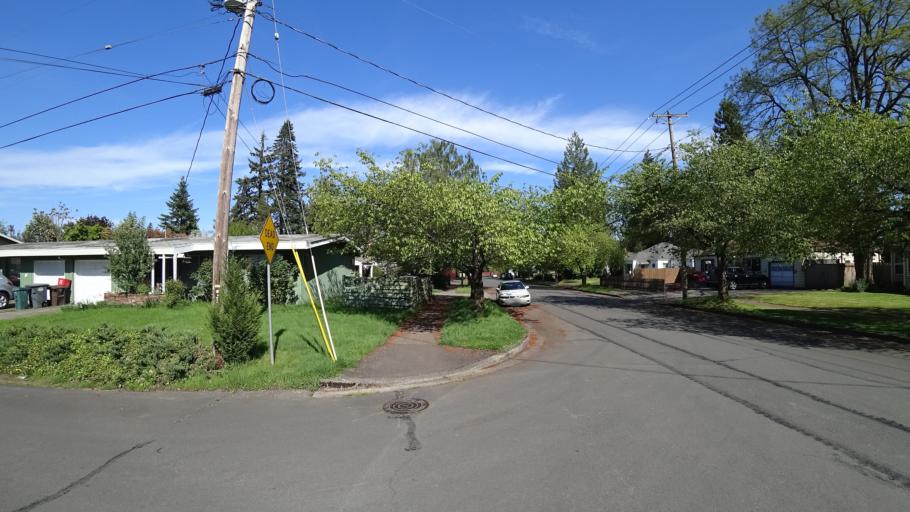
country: US
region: Oregon
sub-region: Washington County
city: Hillsboro
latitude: 45.5251
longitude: -122.9737
